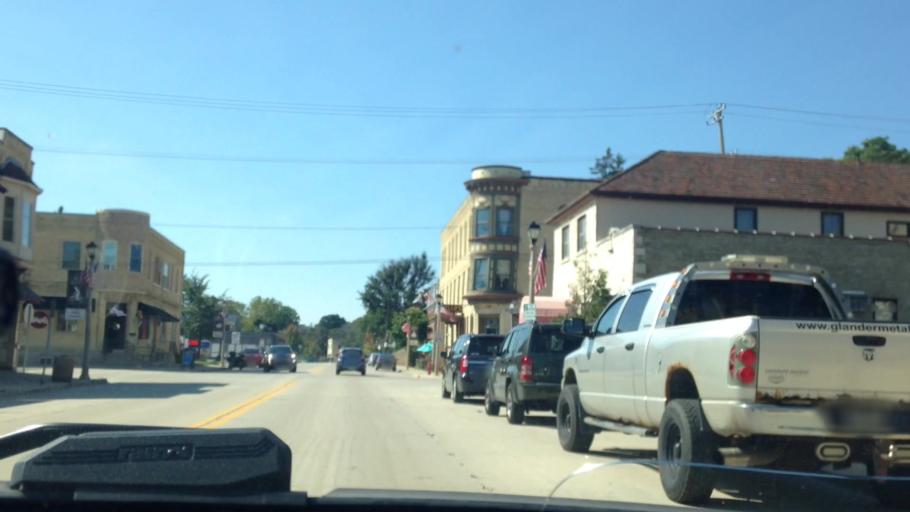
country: US
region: Wisconsin
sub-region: Ozaukee County
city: Port Washington
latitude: 43.3876
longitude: -87.8719
